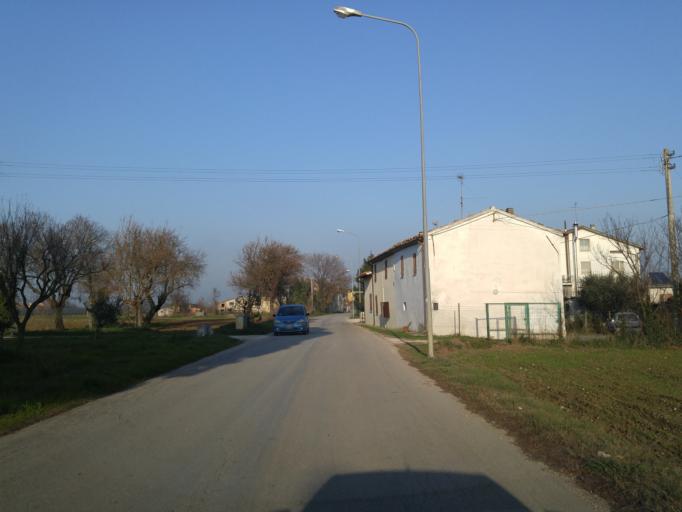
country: IT
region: The Marches
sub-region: Provincia di Pesaro e Urbino
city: Cuccurano
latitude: 43.7829
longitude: 12.9765
